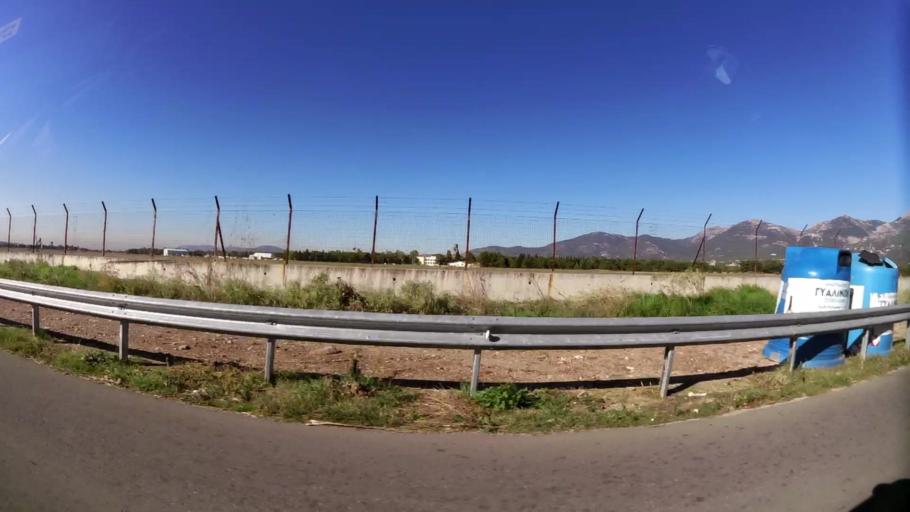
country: GR
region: Attica
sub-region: Nomarchia Anatolikis Attikis
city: Varybobi
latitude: 38.1142
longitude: 23.7898
